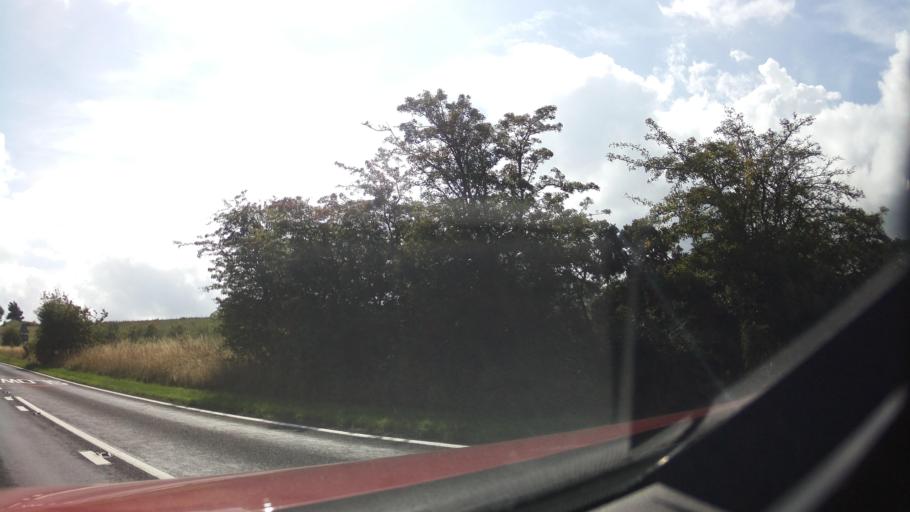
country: GB
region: England
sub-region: Northumberland
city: Healey
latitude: 54.8960
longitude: -1.9416
